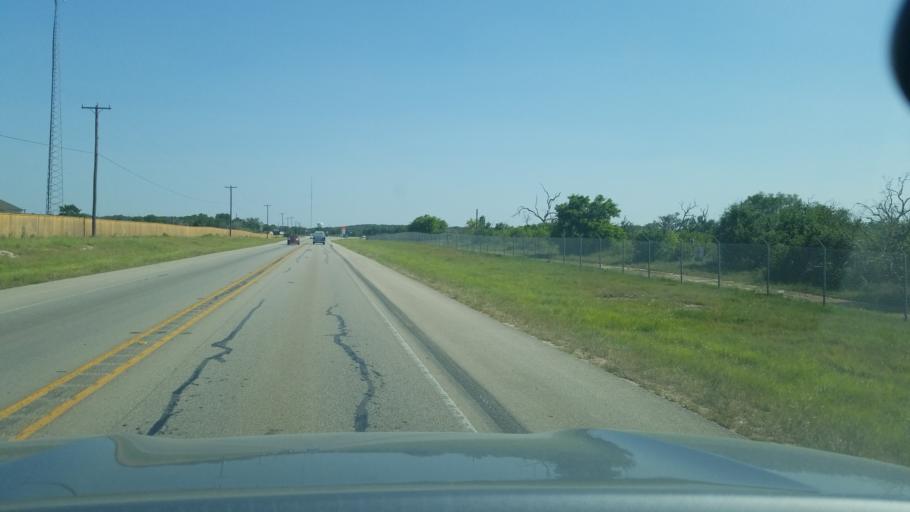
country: US
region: Texas
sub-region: Bexar County
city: Timberwood Park
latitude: 29.7172
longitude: -98.5130
